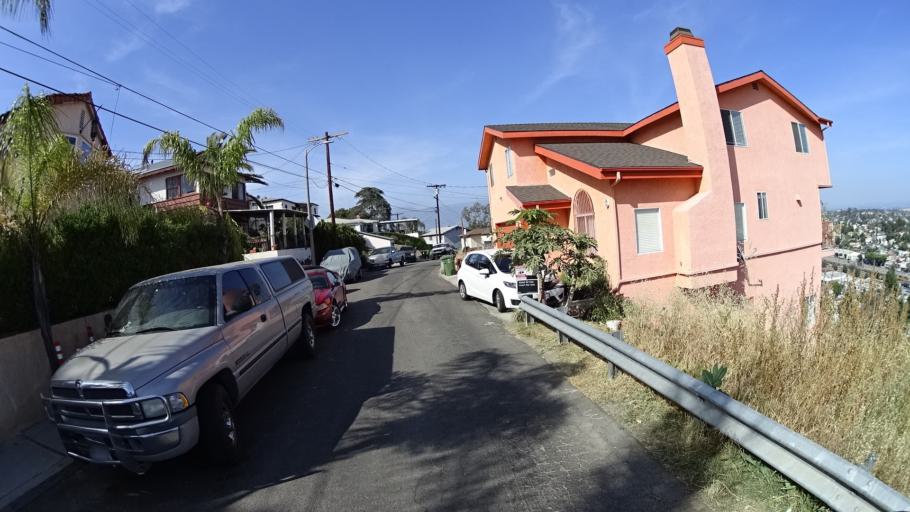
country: US
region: California
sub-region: Los Angeles County
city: Belvedere
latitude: 34.0721
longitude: -118.1774
